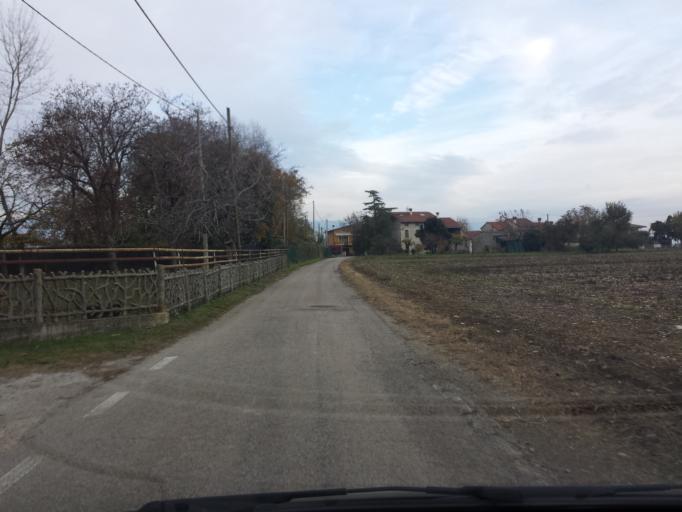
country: IT
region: Veneto
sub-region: Provincia di Vicenza
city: Sandrigo
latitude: 45.6687
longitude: 11.5883
